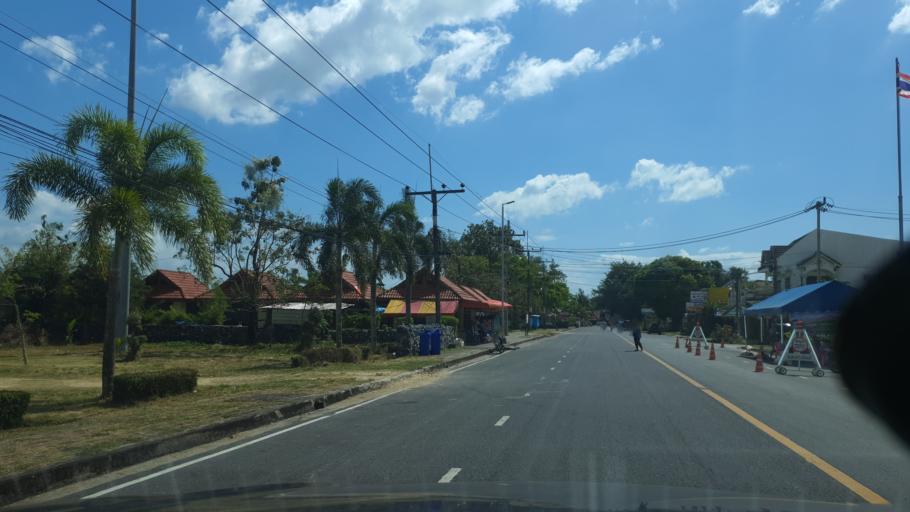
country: TH
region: Phangnga
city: Phang Nga
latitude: 8.3984
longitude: 98.5136
